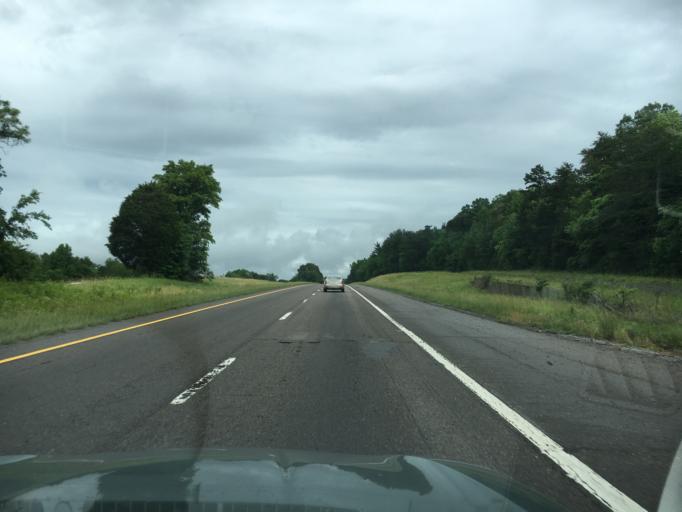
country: US
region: Tennessee
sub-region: Cocke County
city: Newport
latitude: 35.8624
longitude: -83.1841
